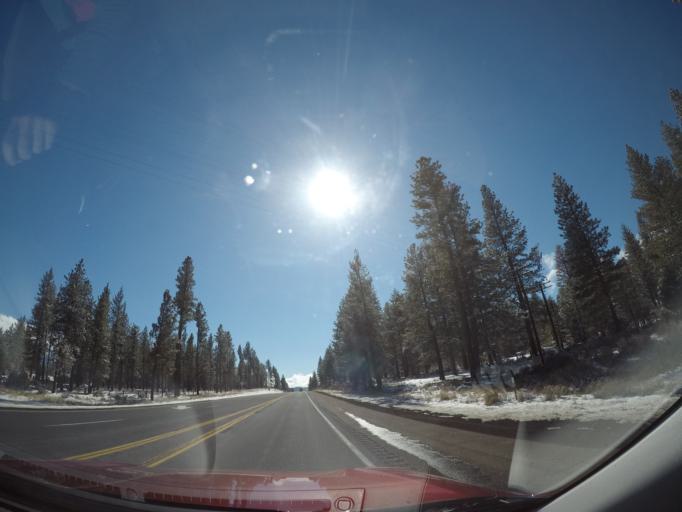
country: US
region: California
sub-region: Siskiyou County
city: Weed
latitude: 41.6307
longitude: -122.1945
